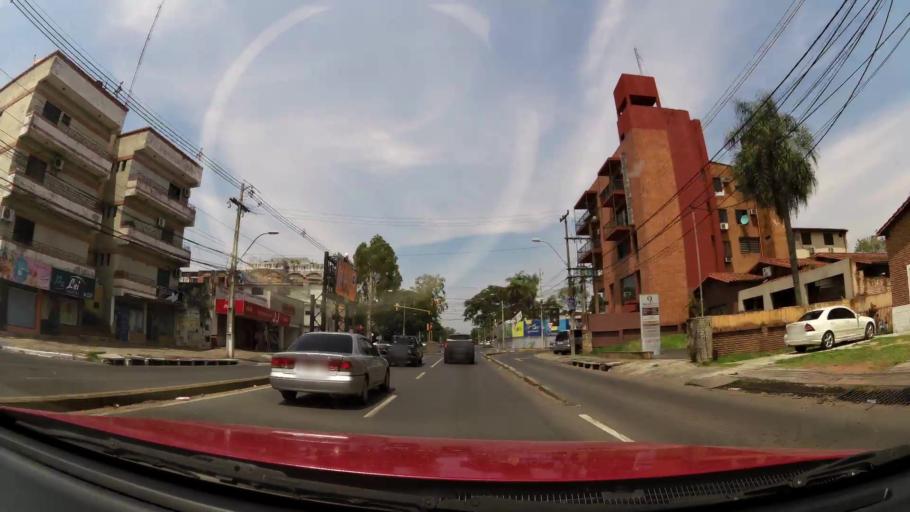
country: PY
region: Asuncion
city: Asuncion
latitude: -25.3010
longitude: -57.5942
